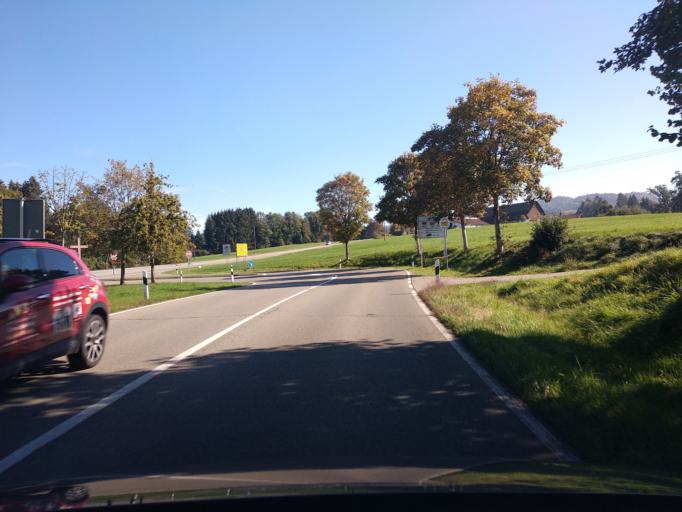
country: AT
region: Vorarlberg
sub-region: Politischer Bezirk Bregenz
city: Hohenweiler
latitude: 47.5964
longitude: 9.7842
